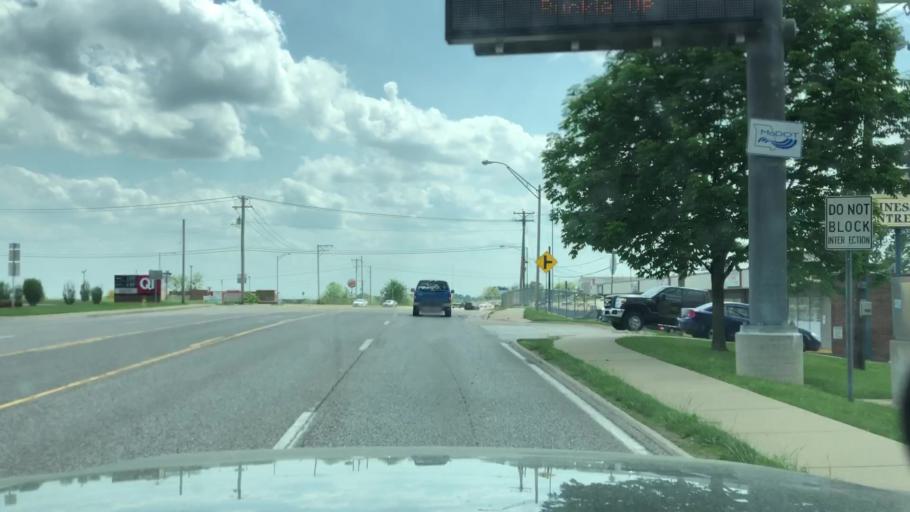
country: US
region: Missouri
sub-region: Saint Charles County
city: Saint Charles
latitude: 38.7791
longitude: -90.5090
